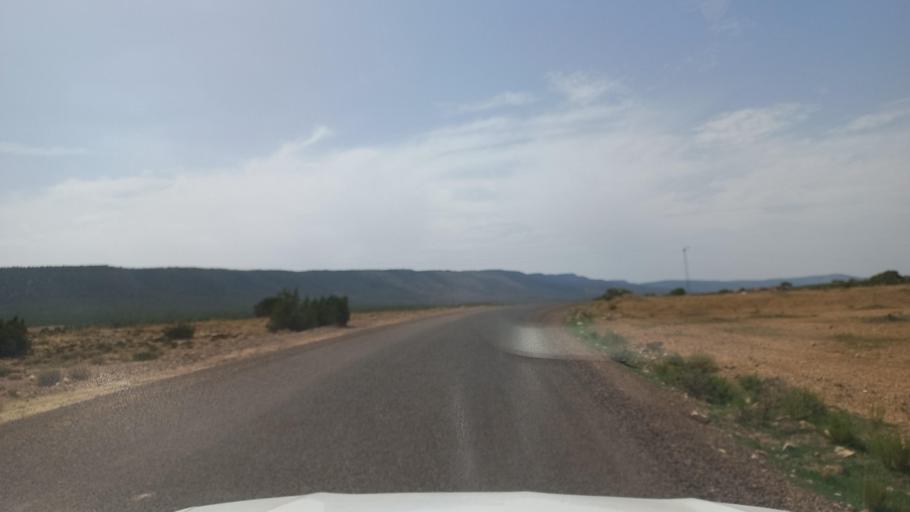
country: TN
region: Al Qasrayn
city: Sbiba
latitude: 35.3904
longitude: 8.9484
